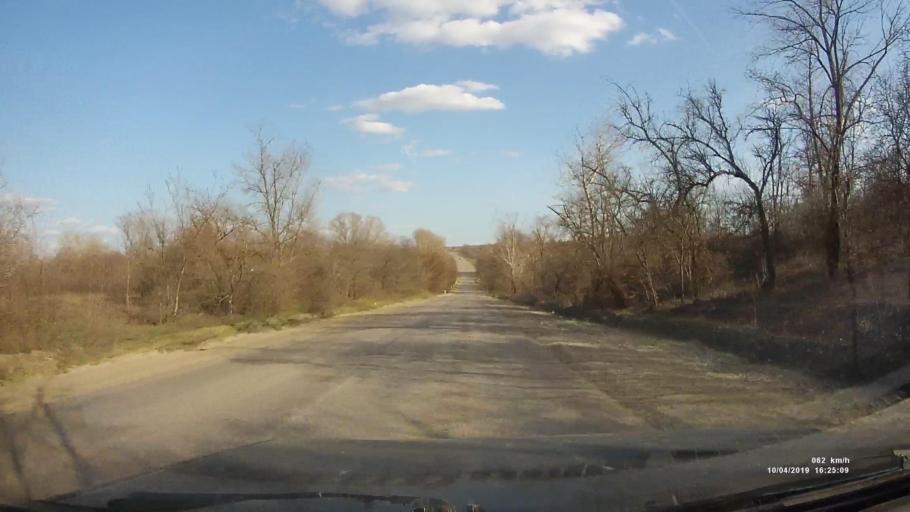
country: RU
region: Rostov
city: Staraya Stanitsa
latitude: 48.2948
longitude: 40.3208
